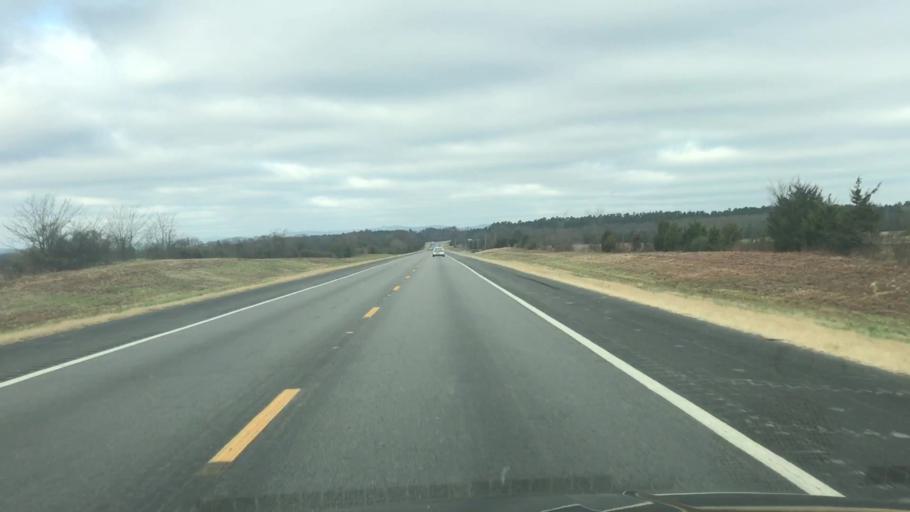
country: US
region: Arkansas
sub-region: Scott County
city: Waldron
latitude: 34.8752
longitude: -94.0918
